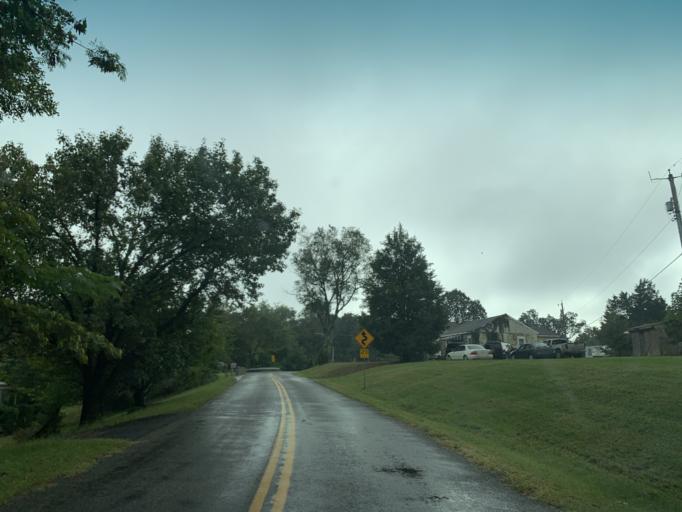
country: US
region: Maryland
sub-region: Harford County
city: Aberdeen
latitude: 39.5654
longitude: -76.1520
